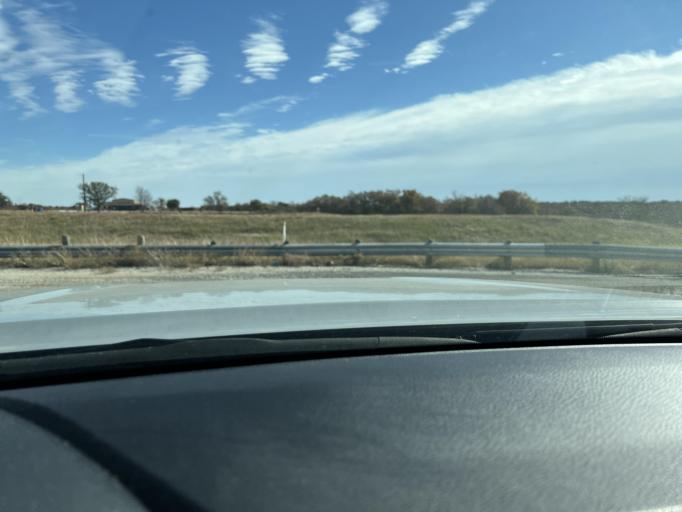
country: US
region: Texas
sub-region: Eastland County
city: Eastland
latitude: 32.3920
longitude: -98.7974
